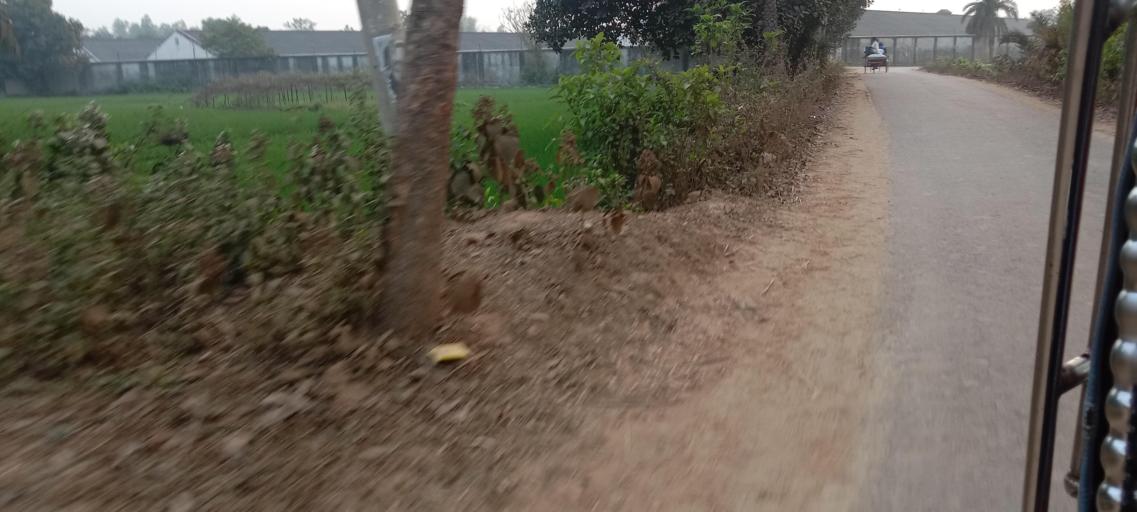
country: BD
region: Dhaka
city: Sakhipur
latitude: 24.4262
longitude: 90.2608
